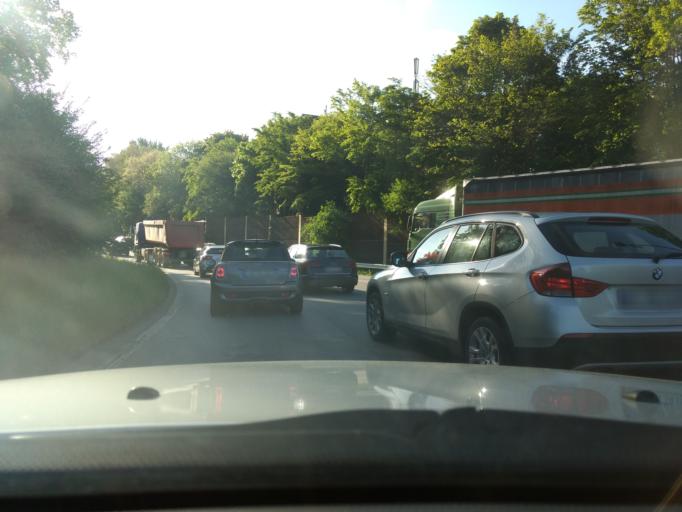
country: DE
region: North Rhine-Westphalia
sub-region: Regierungsbezirk Dusseldorf
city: Neuss
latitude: 51.2344
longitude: 6.7037
